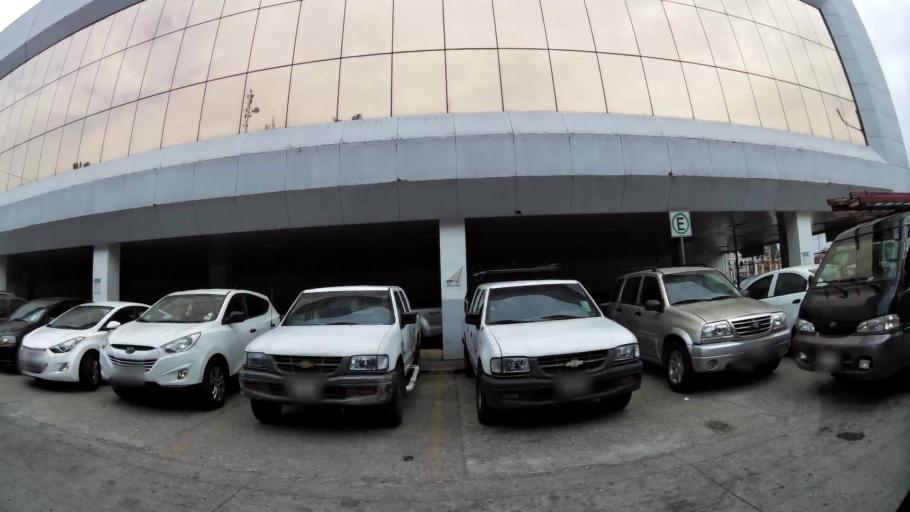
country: EC
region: Guayas
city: Eloy Alfaro
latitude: -2.1459
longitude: -79.8936
